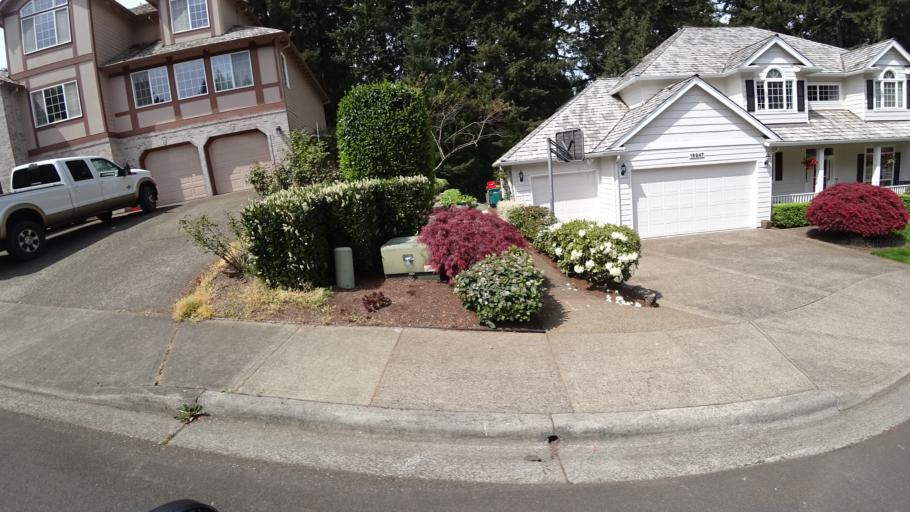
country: US
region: Oregon
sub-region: Washington County
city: Aloha
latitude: 45.4573
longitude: -122.8524
